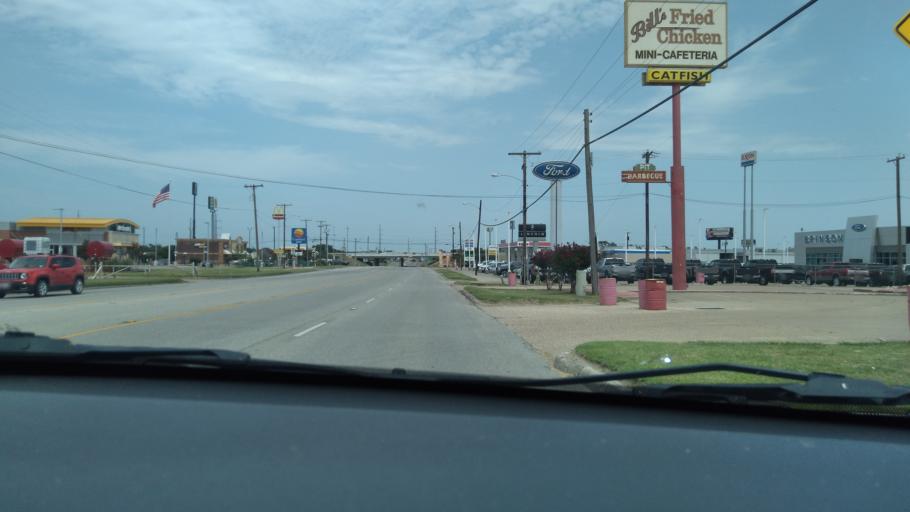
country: US
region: Texas
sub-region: Navarro County
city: Corsicana
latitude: 32.0987
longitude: -96.4448
